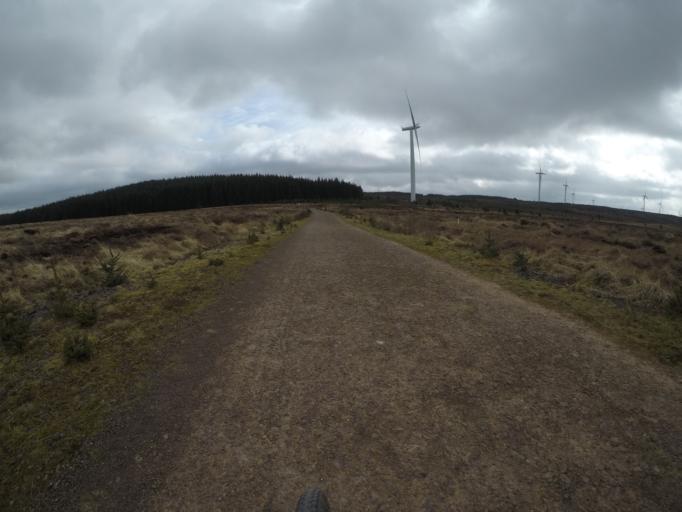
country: GB
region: Scotland
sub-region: East Renfrewshire
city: Eaglesham
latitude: 55.7074
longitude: -4.2977
